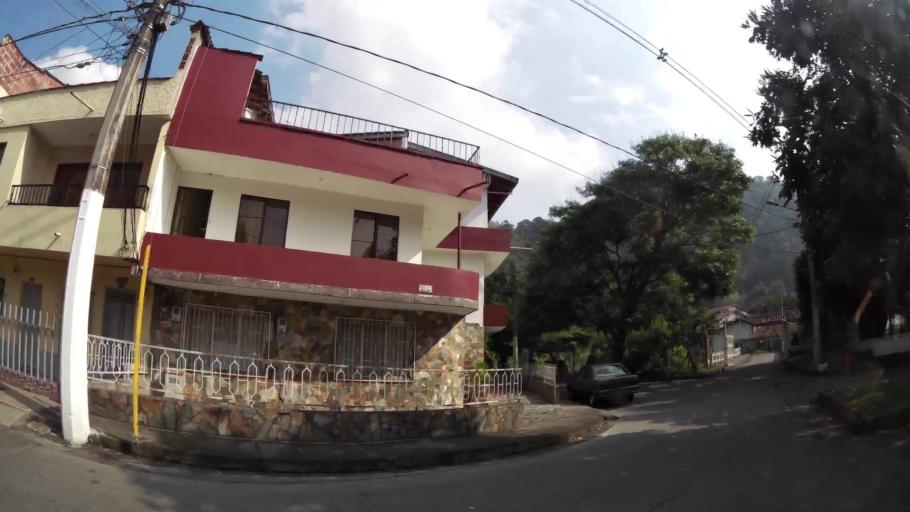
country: CO
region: Antioquia
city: Sabaneta
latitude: 6.1724
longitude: -75.6257
